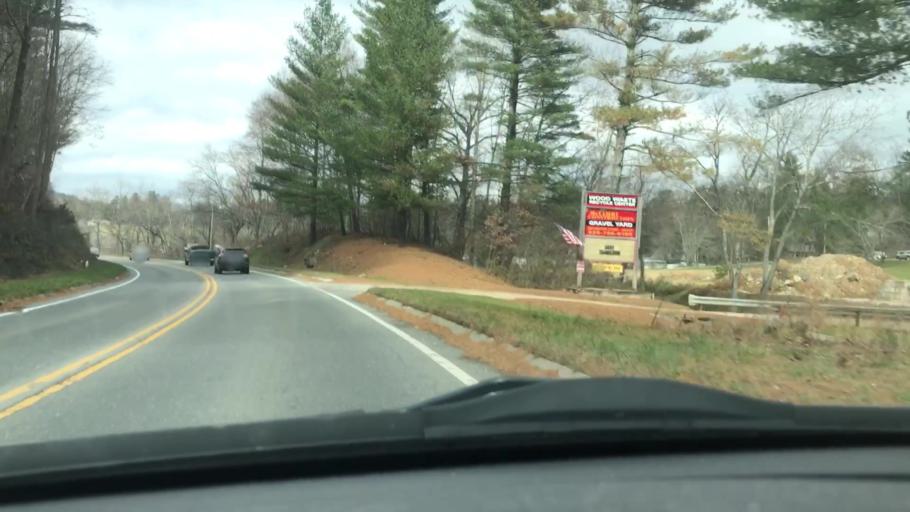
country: US
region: North Carolina
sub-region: Mitchell County
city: Spruce Pine
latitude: 35.8857
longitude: -82.0587
